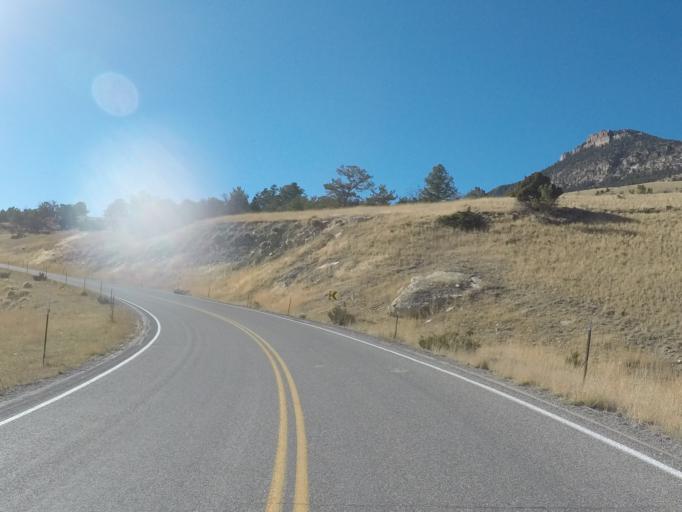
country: US
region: Wyoming
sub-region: Park County
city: Cody
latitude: 44.7722
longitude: -109.4266
